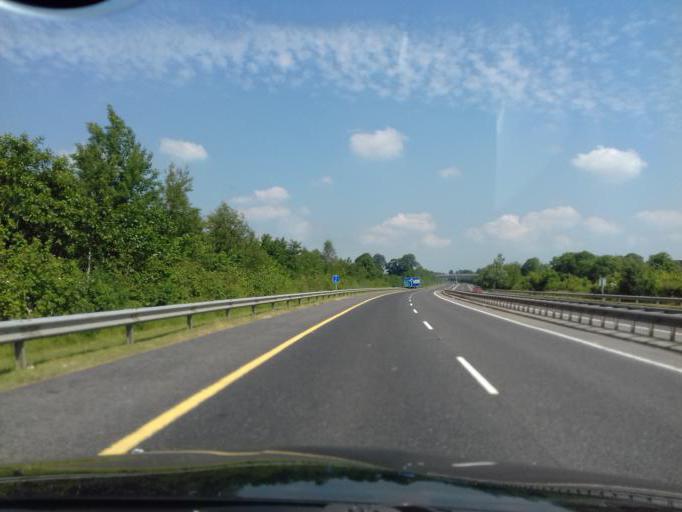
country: IE
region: Leinster
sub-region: An Mhi
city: Ashbourne
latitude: 53.5121
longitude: -6.4210
